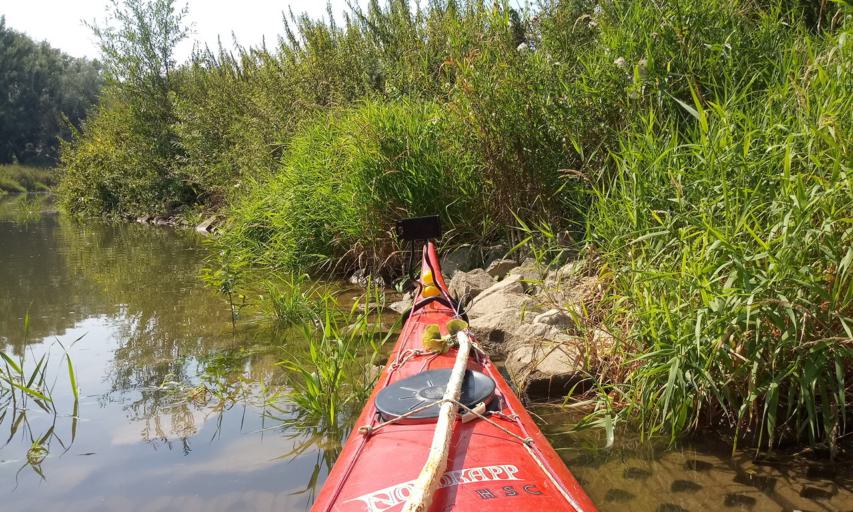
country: NL
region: Gelderland
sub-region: Gemeente Brummen
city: Brummen
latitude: 52.0668
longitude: 6.1478
